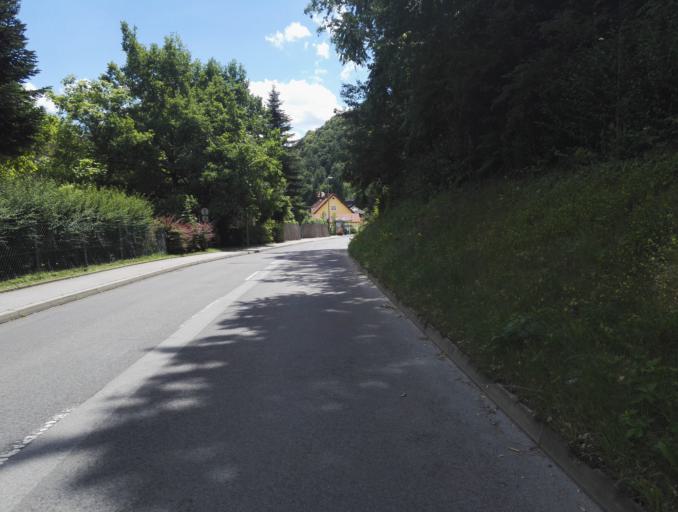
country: AT
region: Styria
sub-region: Graz Stadt
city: Goesting
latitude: 47.0924
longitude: 15.3970
